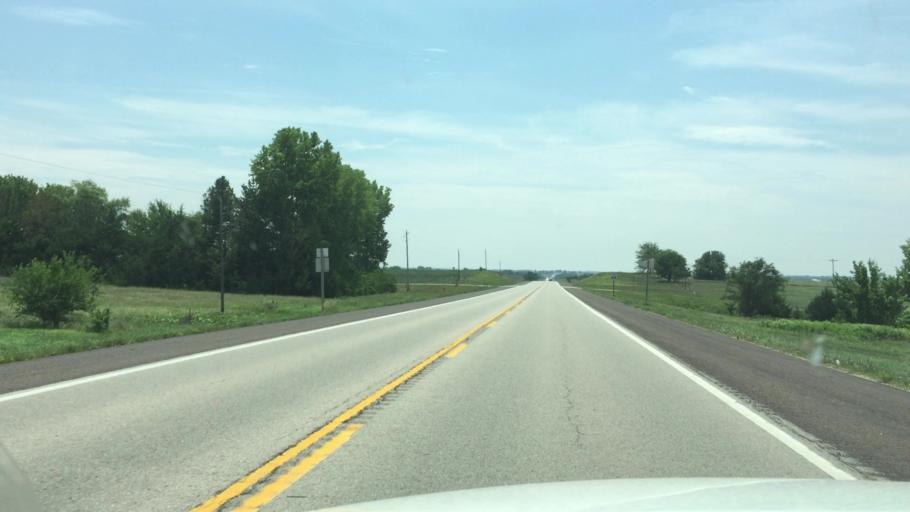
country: US
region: Kansas
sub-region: Jackson County
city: Holton
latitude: 39.6110
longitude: -95.7313
